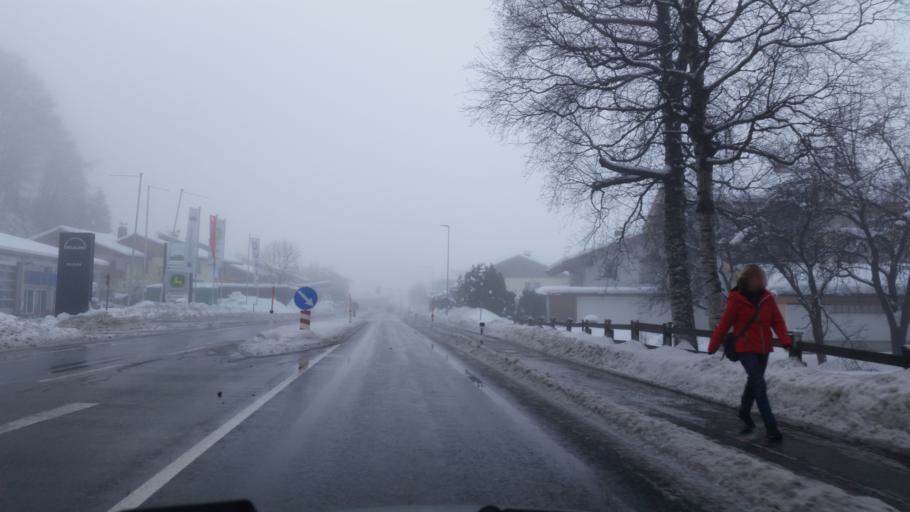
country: AT
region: Tyrol
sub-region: Politischer Bezirk Kitzbuhel
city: Kirchdorf in Tirol
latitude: 47.5443
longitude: 12.4488
